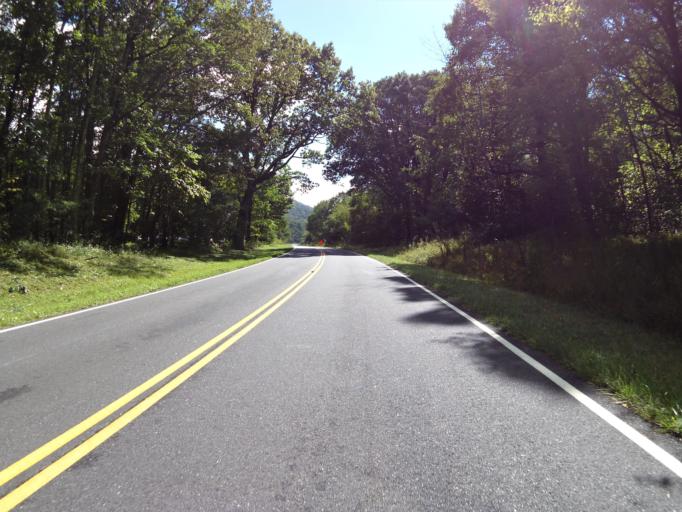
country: US
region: Virginia
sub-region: Page County
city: Luray
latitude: 38.6999
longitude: -78.3208
